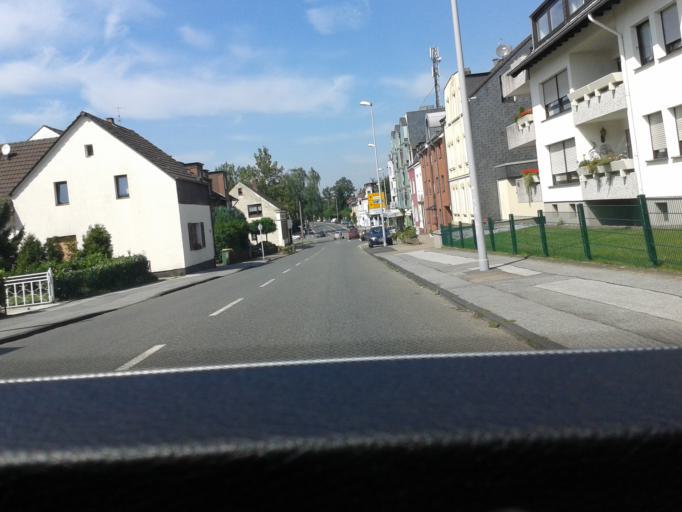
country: DE
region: North Rhine-Westphalia
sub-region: Regierungsbezirk Dusseldorf
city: Muelheim (Ruhr)
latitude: 51.4127
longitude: 6.8597
